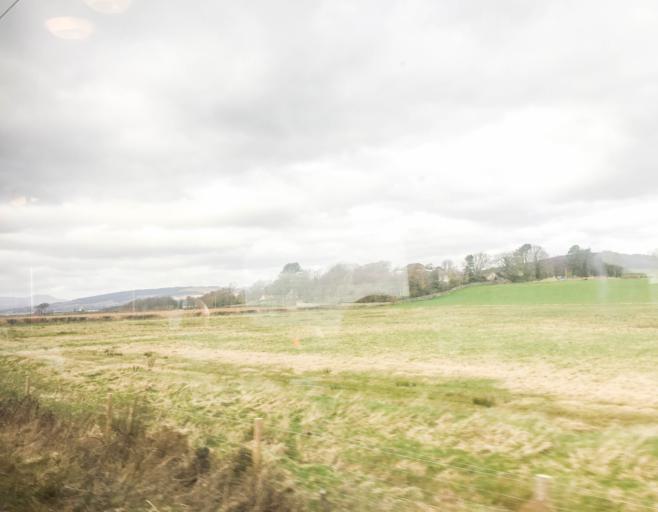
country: GB
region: Scotland
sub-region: Inverclyde
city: Port Glasgow
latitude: 55.9631
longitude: -4.6708
